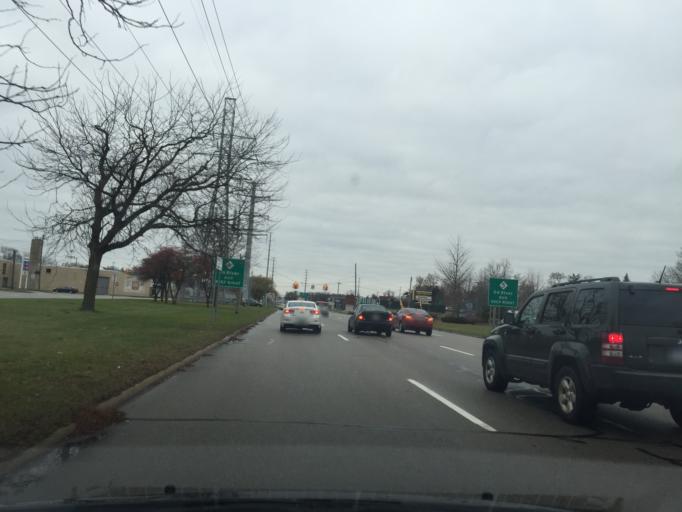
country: US
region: Michigan
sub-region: Wayne County
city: Redford
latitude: 42.4422
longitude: -83.3152
